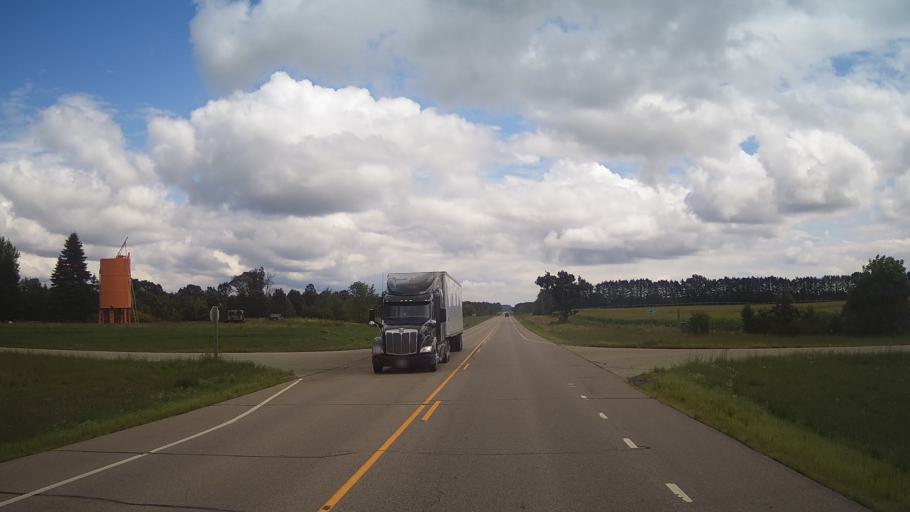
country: US
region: Wisconsin
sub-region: Adams County
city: Friendship
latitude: 44.0220
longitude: -89.6390
